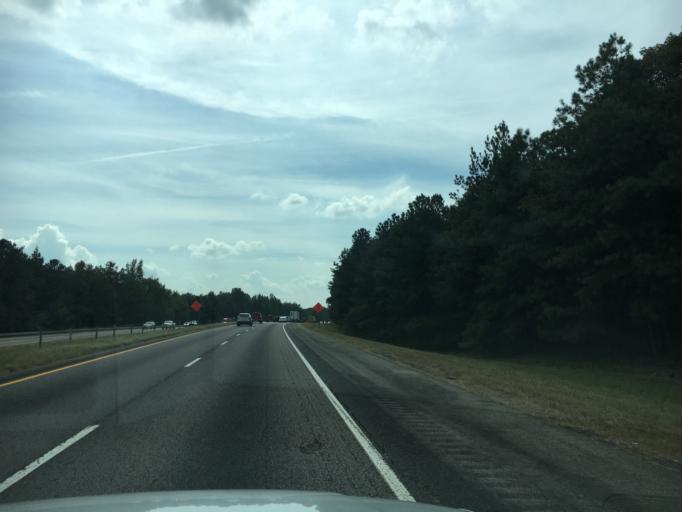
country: US
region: Georgia
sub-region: Barrow County
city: Auburn
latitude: 34.0874
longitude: -83.8434
